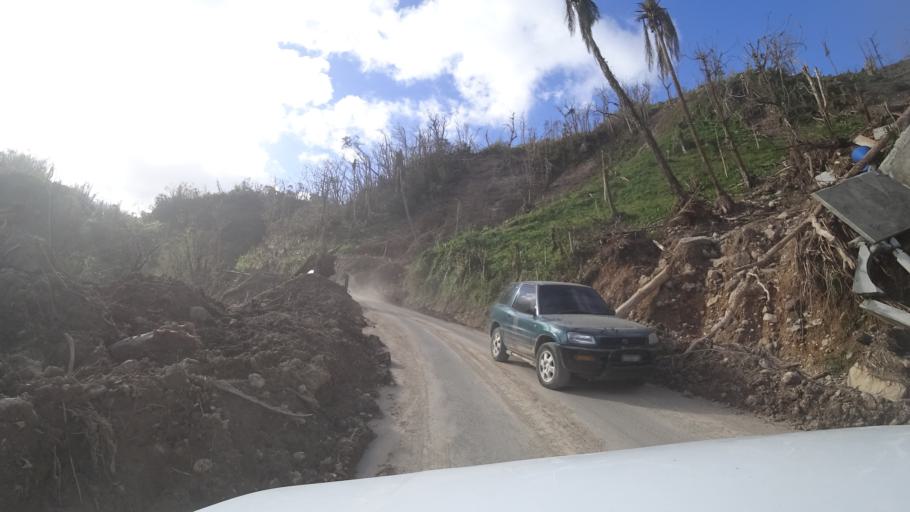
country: DM
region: Saint Patrick
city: Berekua
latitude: 15.2650
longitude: -61.3329
